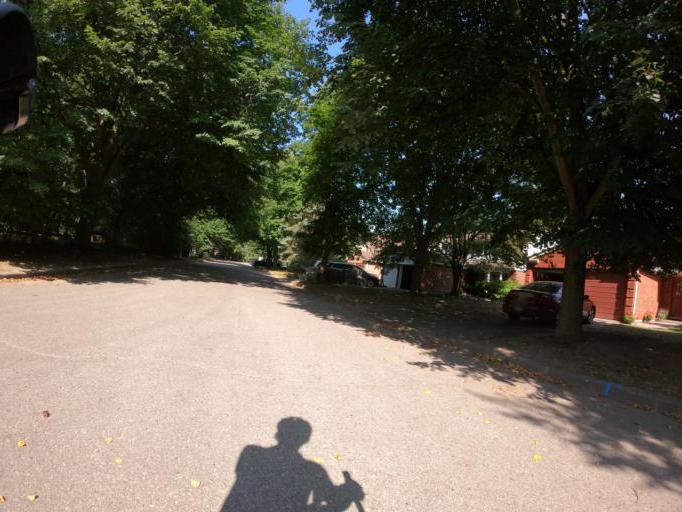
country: CA
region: Ontario
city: Waterloo
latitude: 43.4636
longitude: -80.5582
